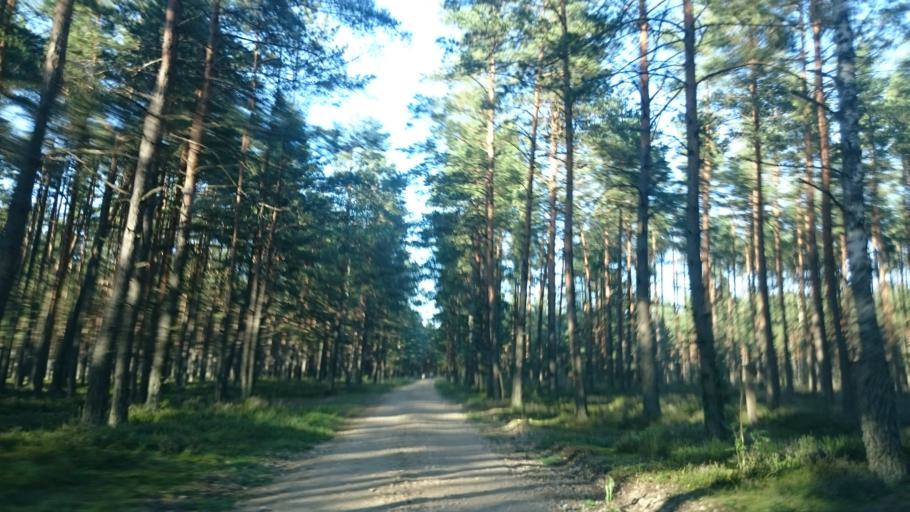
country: LV
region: Carnikava
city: Carnikava
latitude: 57.1071
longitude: 24.2359
